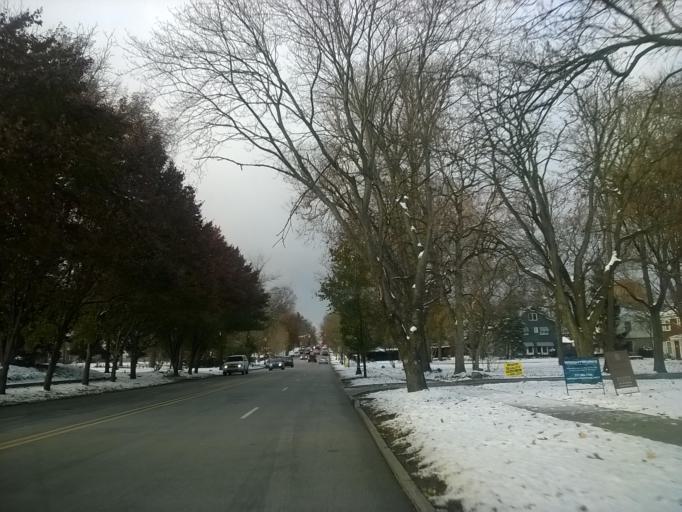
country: US
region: Indiana
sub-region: Marion County
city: Broad Ripple
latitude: 39.8368
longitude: -86.1569
